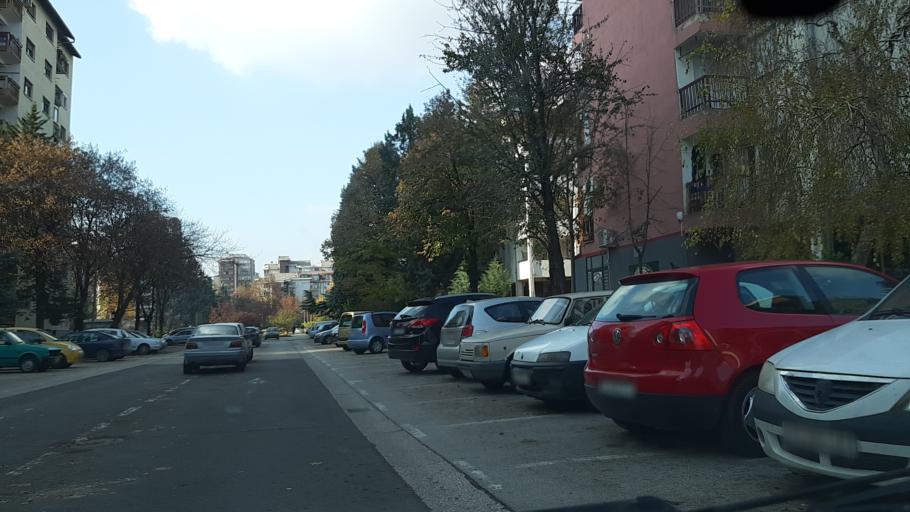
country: MK
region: Kisela Voda
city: Usje
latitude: 41.9817
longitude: 21.4683
